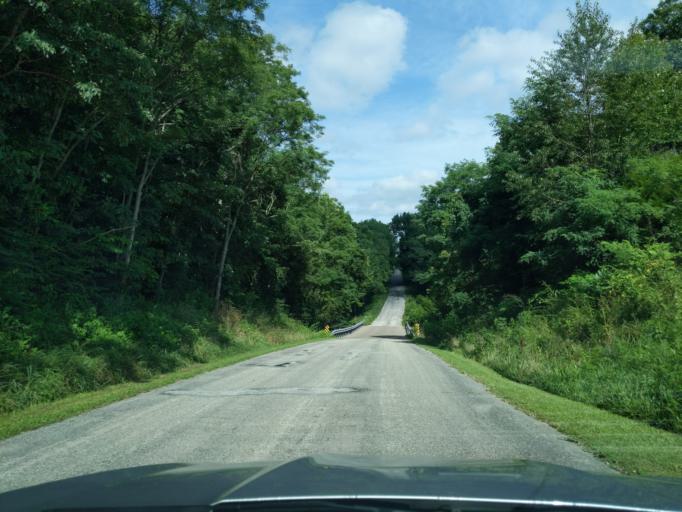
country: US
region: Indiana
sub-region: Decatur County
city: Greensburg
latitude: 39.2350
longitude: -85.3997
